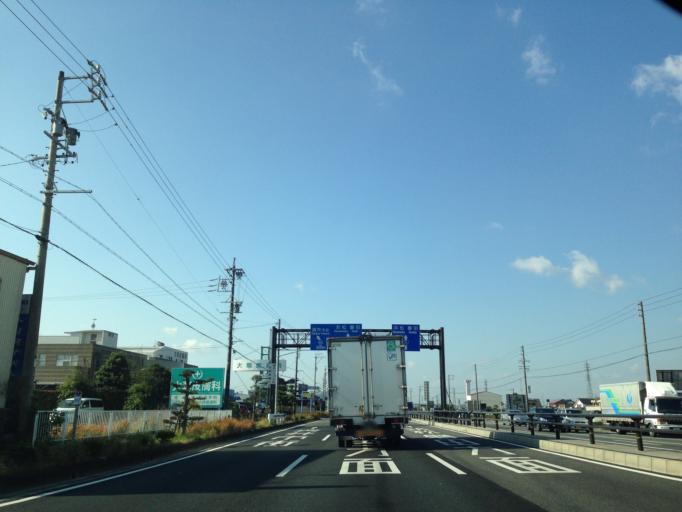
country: JP
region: Shizuoka
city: Fukuroi
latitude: 34.7601
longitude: 137.9456
